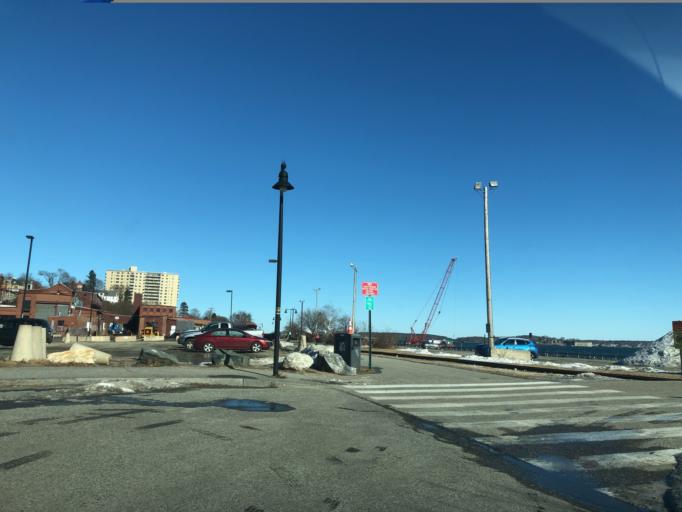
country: US
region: Maine
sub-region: Cumberland County
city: Portland
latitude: 43.6610
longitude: -70.2460
